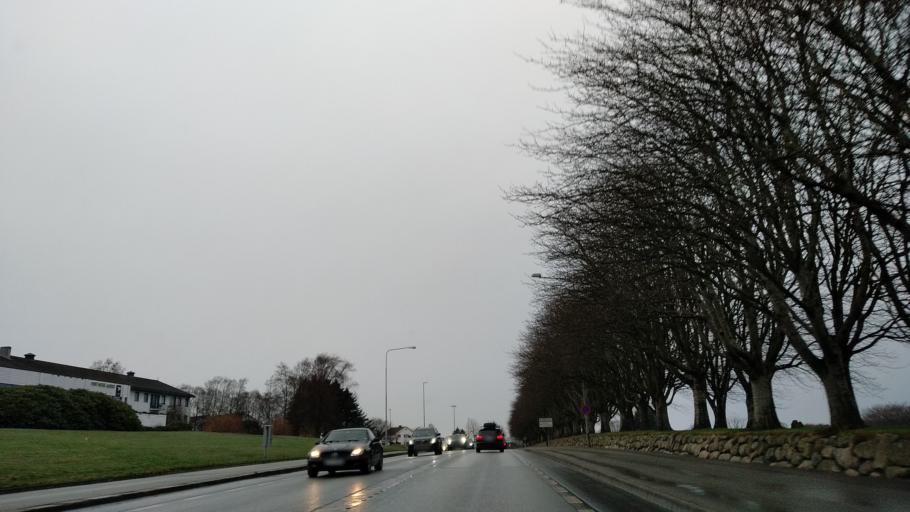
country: NO
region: Rogaland
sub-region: Stavanger
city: Stavanger
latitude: 58.9529
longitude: 5.7083
